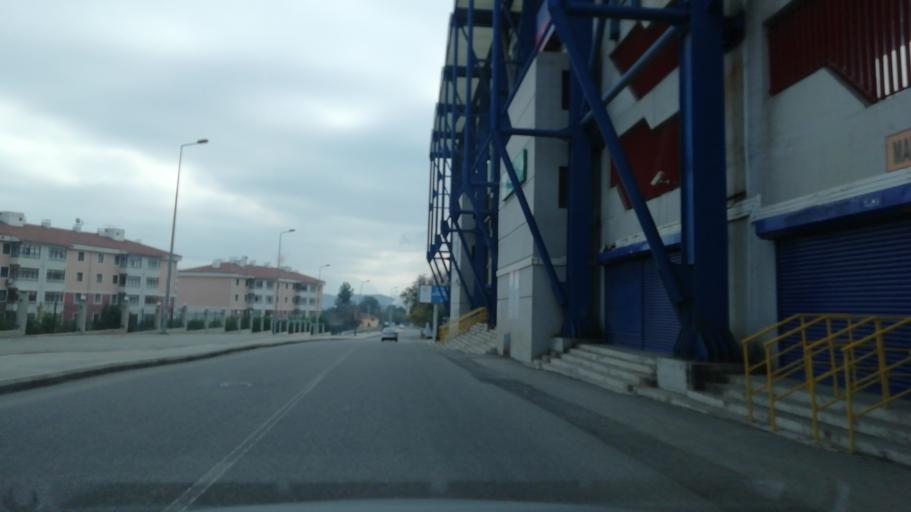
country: TR
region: Karabuk
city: Karabuk
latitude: 41.2049
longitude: 32.6207
